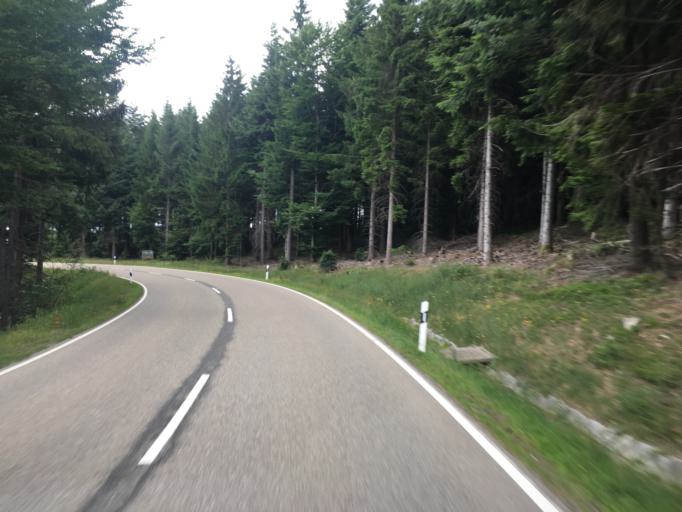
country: DE
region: Baden-Wuerttemberg
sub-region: Karlsruhe Region
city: Buhlertal
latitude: 48.6659
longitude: 8.2345
